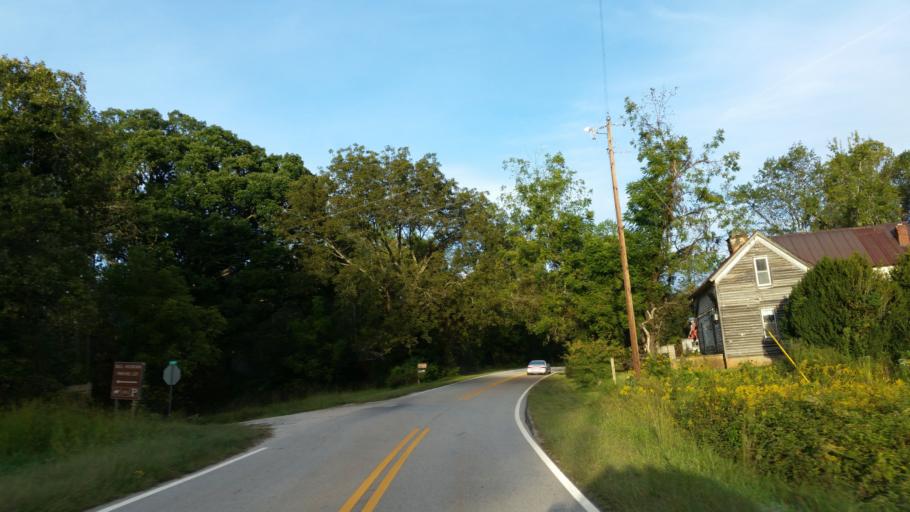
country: US
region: Georgia
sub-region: Dawson County
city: Dawsonville
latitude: 34.5644
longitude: -84.1387
